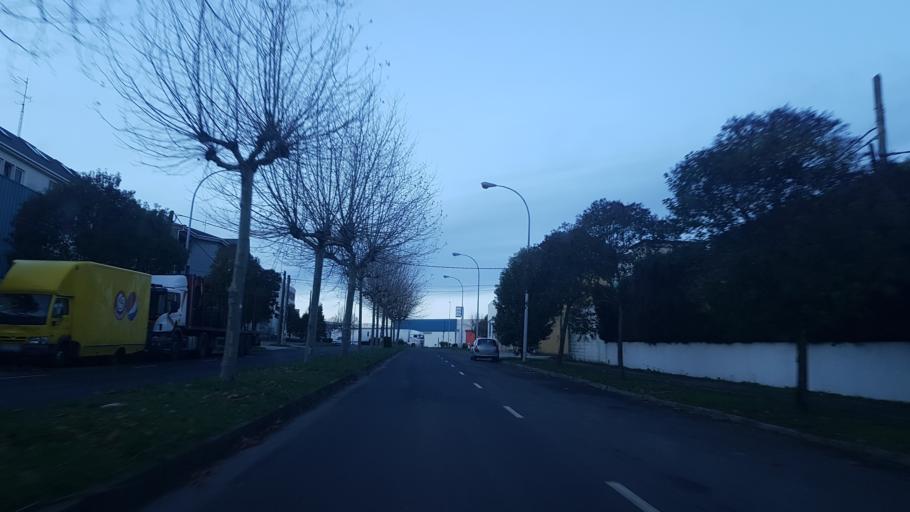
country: ES
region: Galicia
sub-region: Provincia de Lugo
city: Lugo
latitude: 43.0458
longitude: -7.5711
